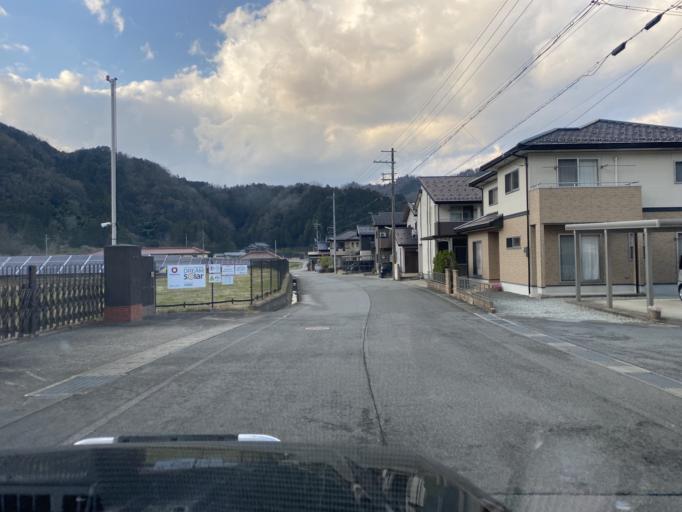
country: JP
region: Hyogo
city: Toyooka
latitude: 35.4651
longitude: 134.7590
